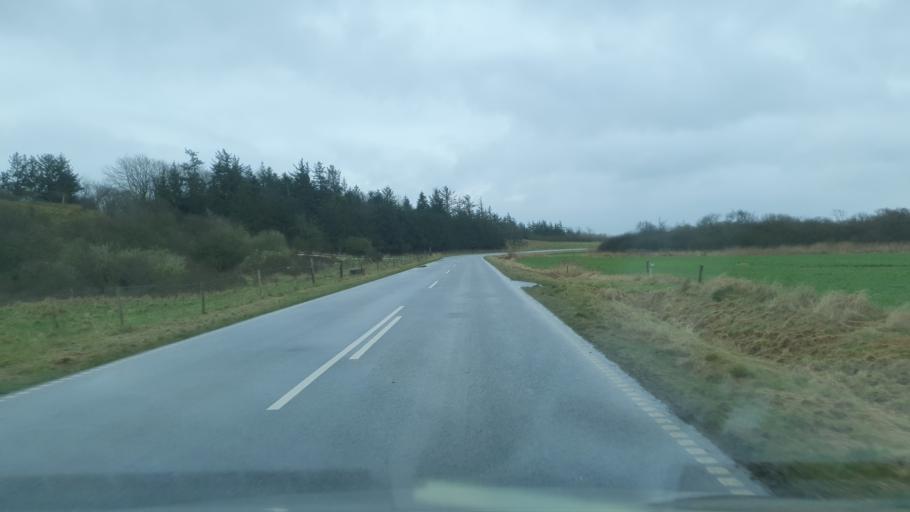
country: DK
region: North Denmark
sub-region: Jammerbugt Kommune
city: Fjerritslev
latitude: 57.1159
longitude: 9.1276
